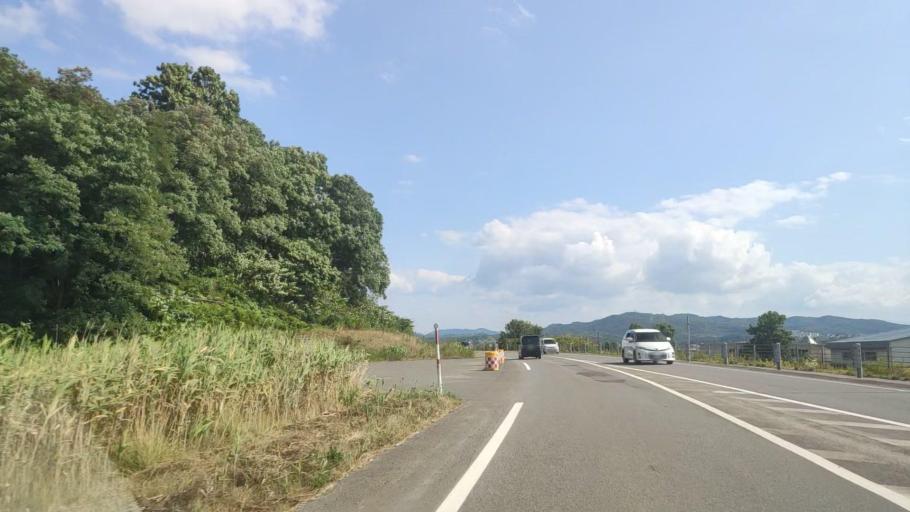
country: JP
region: Hokkaido
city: Rumoi
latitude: 43.9517
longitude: 141.6457
